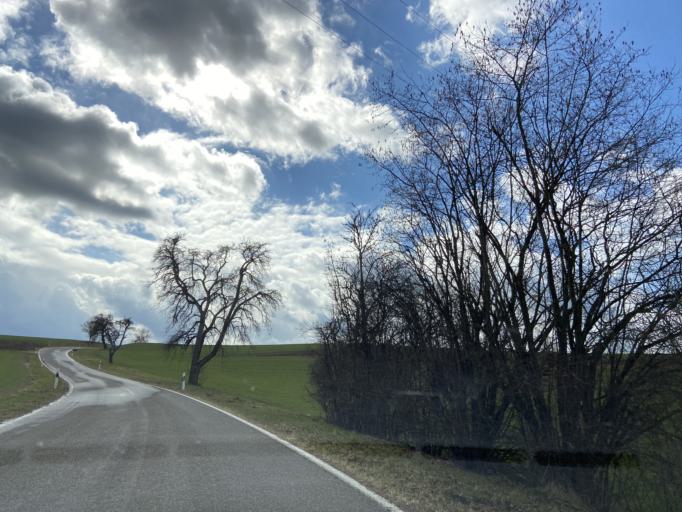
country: DE
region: Baden-Wuerttemberg
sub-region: Tuebingen Region
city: Mengen
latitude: 47.9902
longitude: 9.3222
